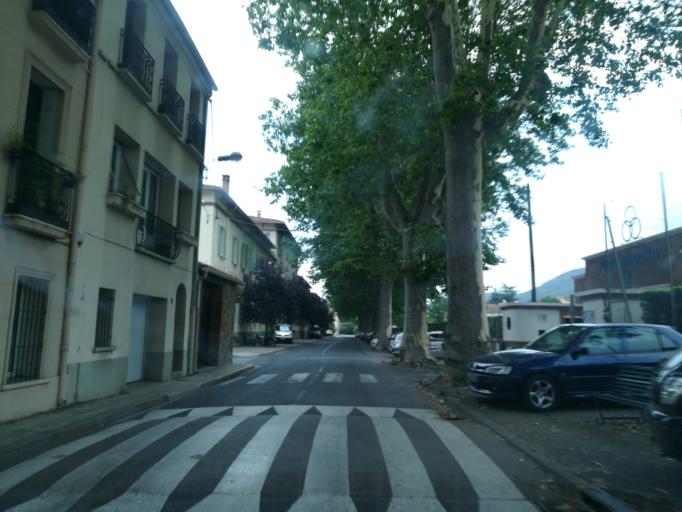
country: FR
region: Languedoc-Roussillon
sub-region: Departement des Pyrenees-Orientales
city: Ceret
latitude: 42.4847
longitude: 2.7518
